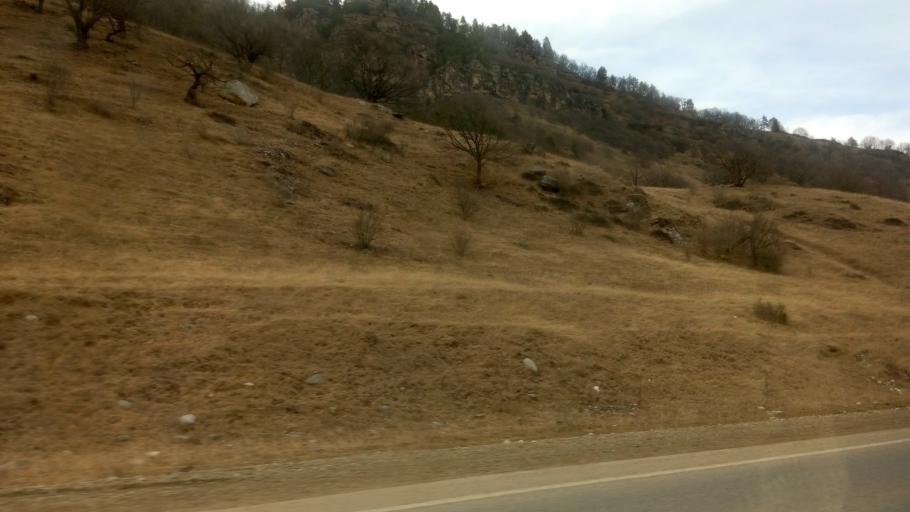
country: RU
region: Karachayevo-Cherkesiya
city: Teberda
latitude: 43.5816
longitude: 41.8438
